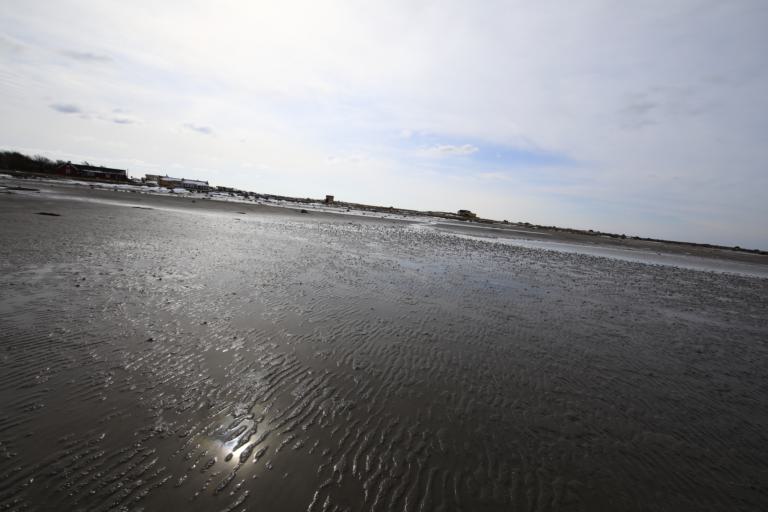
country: SE
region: Halland
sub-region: Varbergs Kommun
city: Traslovslage
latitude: 57.0739
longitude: 12.2560
